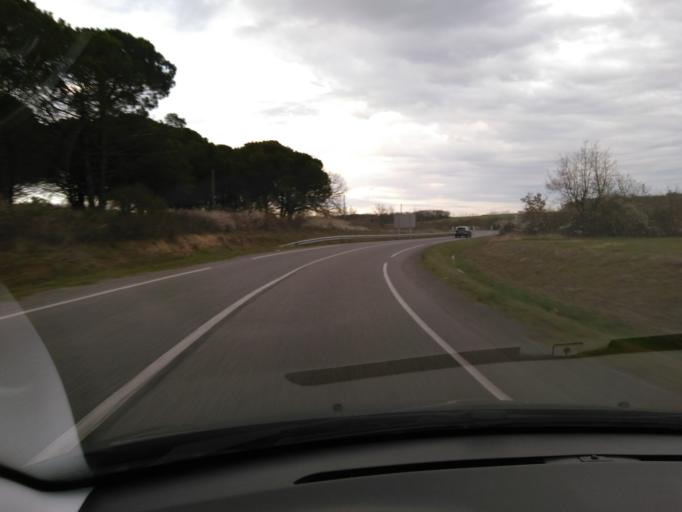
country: FR
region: Midi-Pyrenees
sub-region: Departement de la Haute-Garonne
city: La Salvetat-Saint-Gilles
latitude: 43.5895
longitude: 1.2696
